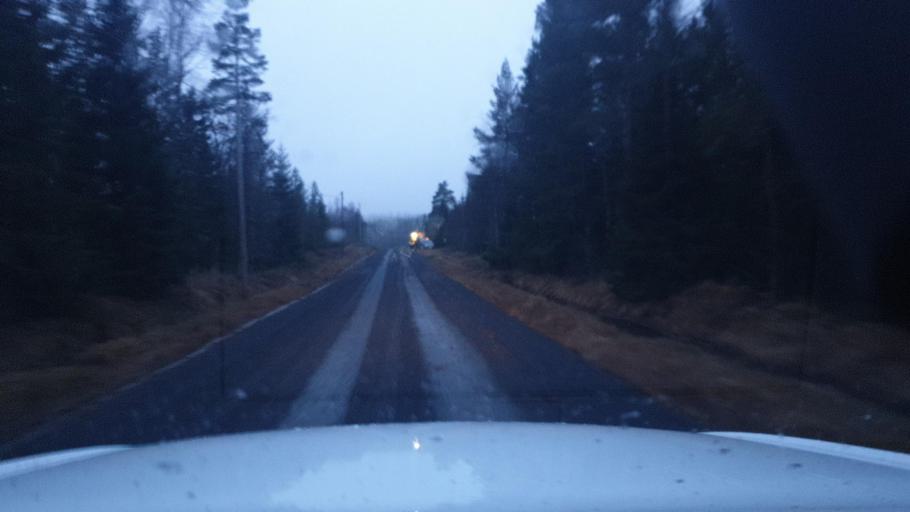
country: SE
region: Vaermland
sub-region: Torsby Kommun
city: Torsby
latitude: 60.1661
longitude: 12.6187
